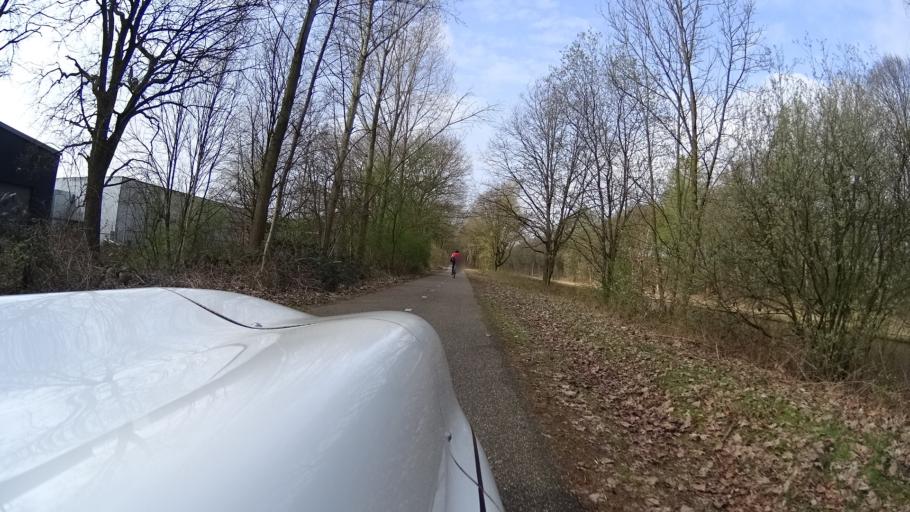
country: NL
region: North Brabant
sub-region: Gemeente Son en Breugel
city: Son
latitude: 51.5042
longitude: 5.4649
